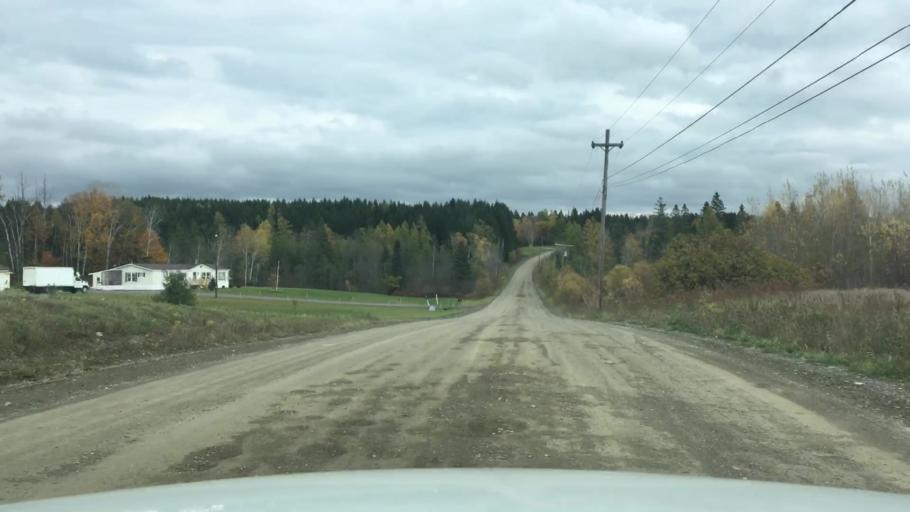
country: US
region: Maine
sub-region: Aroostook County
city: Easton
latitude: 46.5229
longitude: -67.8930
